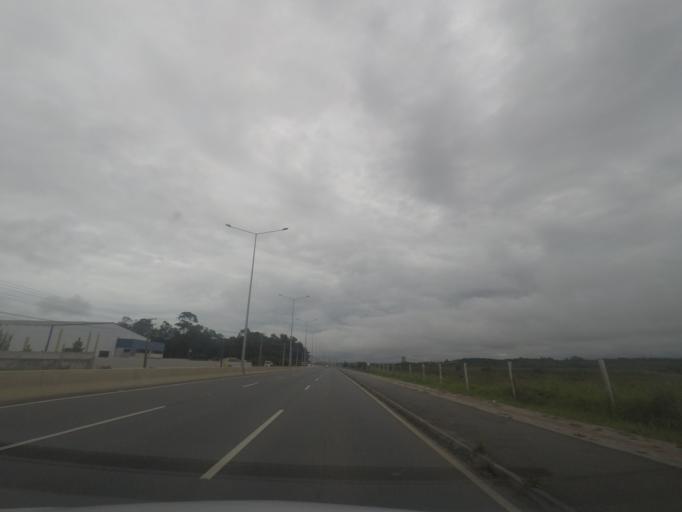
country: BR
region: Parana
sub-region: Pinhais
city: Pinhais
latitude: -25.4473
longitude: -49.1337
